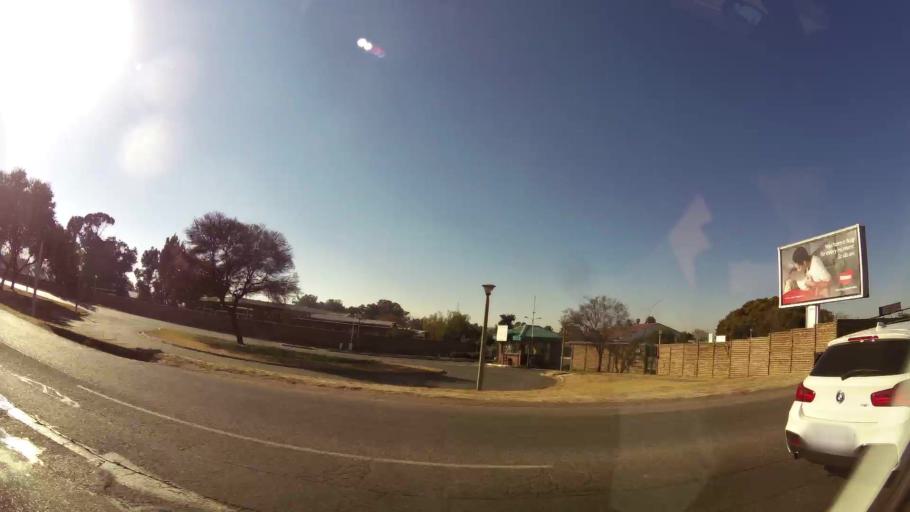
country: ZA
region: Gauteng
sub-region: Ekurhuleni Metropolitan Municipality
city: Germiston
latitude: -26.2853
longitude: 28.1210
